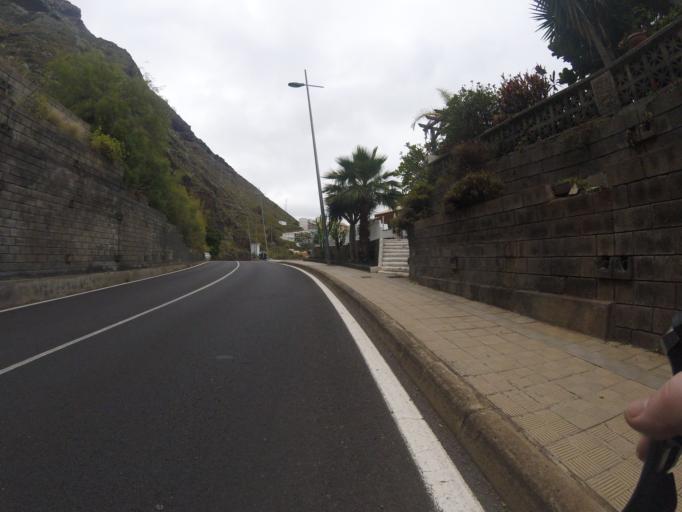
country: ES
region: Canary Islands
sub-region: Provincia de Santa Cruz de Tenerife
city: Tegueste
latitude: 28.5561
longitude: -16.3354
